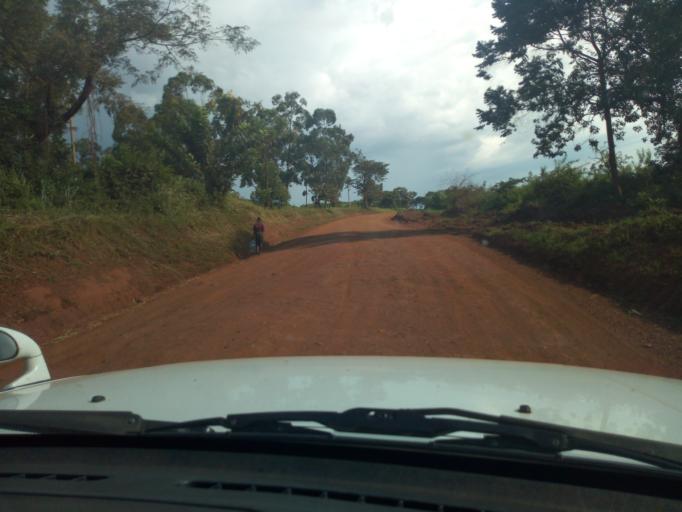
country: UG
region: Western Region
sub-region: Masindi District
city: Masindi
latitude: 1.6571
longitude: 31.7061
